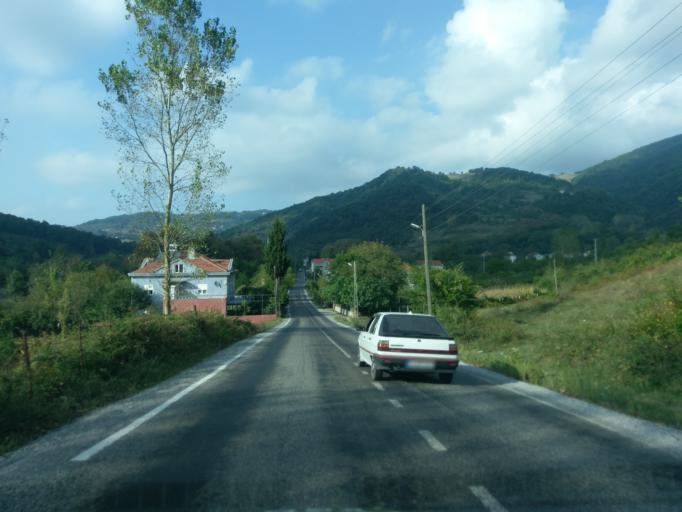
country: TR
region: Sinop
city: Helaldi
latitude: 41.9217
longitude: 34.4138
